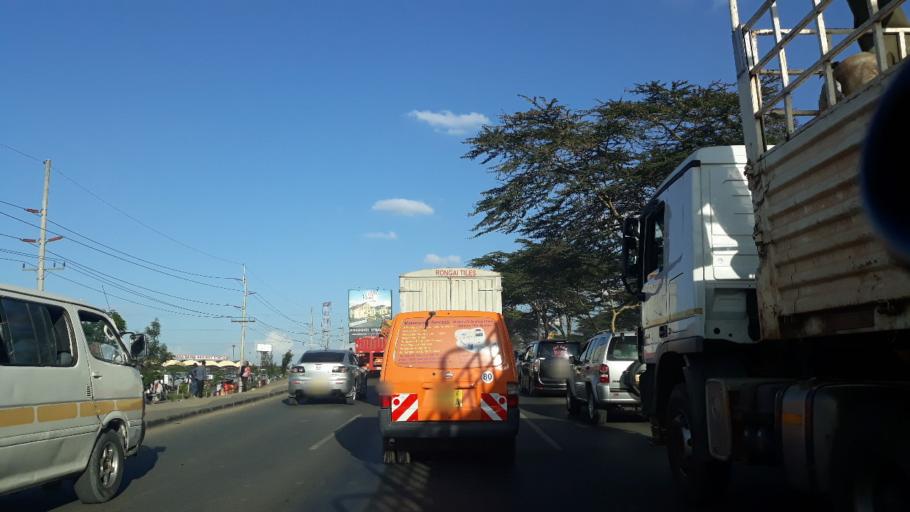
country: KE
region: Nairobi Area
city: Pumwani
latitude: -1.3296
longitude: 36.8722
